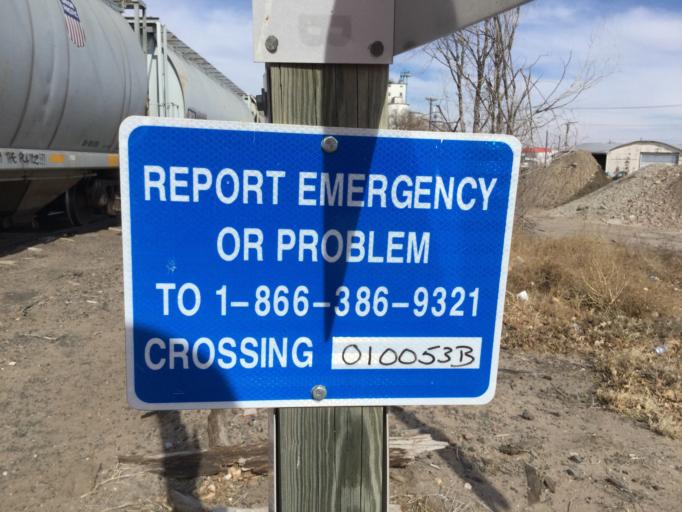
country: US
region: Kansas
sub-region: Pawnee County
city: Larned
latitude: 38.1744
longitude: -99.1013
